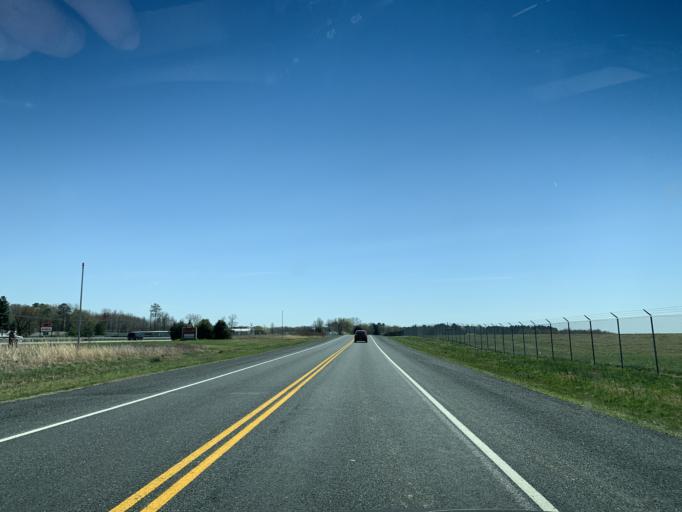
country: US
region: Maryland
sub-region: Talbot County
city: Easton
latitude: 38.8122
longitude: -76.0608
